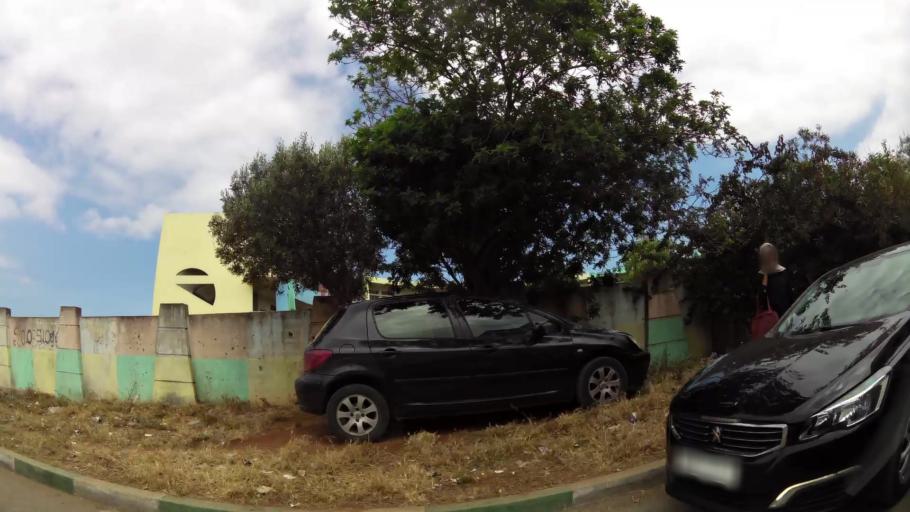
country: MA
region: Rabat-Sale-Zemmour-Zaer
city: Sale
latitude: 34.0639
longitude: -6.7868
